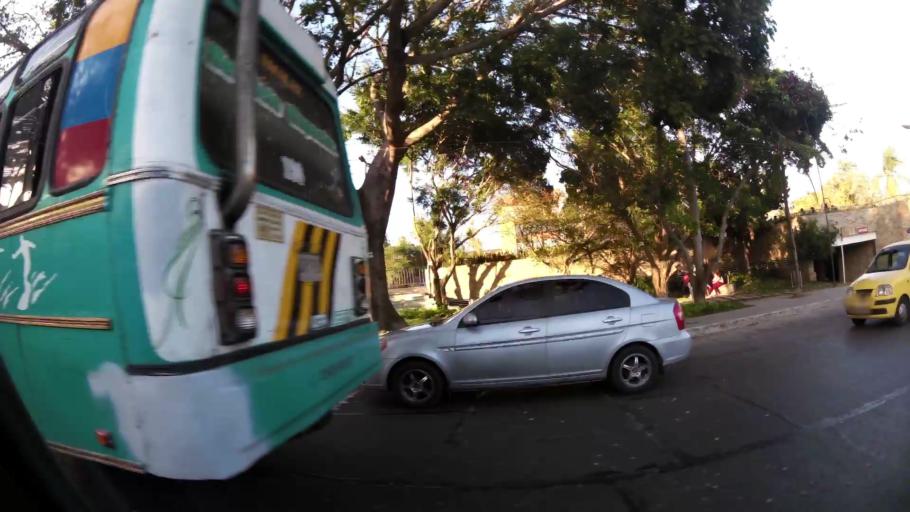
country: CO
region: Atlantico
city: Barranquilla
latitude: 10.9876
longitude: -74.7892
